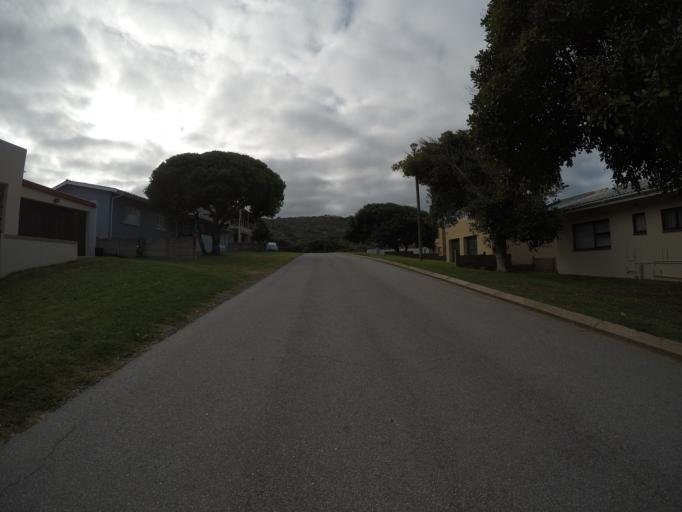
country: ZA
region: Western Cape
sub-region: Eden District Municipality
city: Riversdale
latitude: -34.4261
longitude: 21.3352
